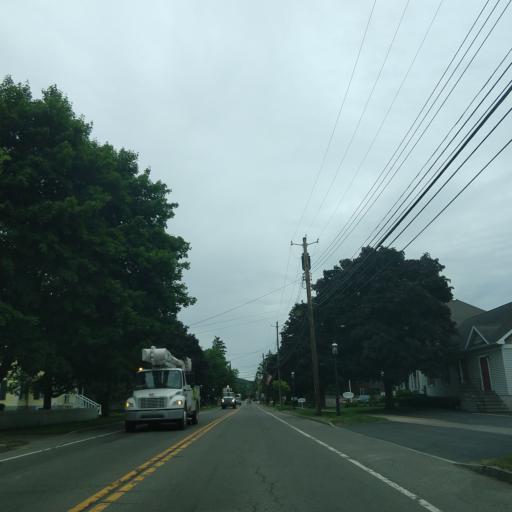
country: US
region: New York
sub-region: Tompkins County
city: Dryden
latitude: 42.4903
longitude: -76.3034
